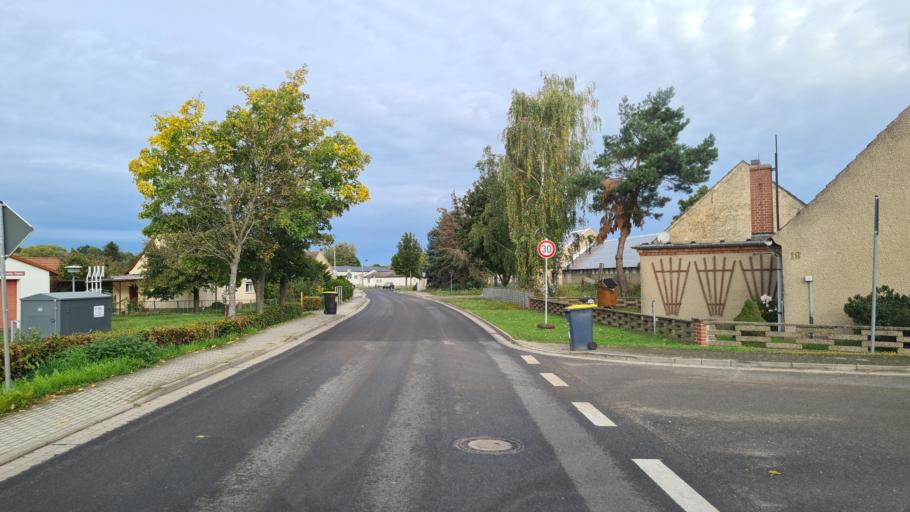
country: DE
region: Brandenburg
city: Luckau
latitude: 51.8698
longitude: 13.7258
